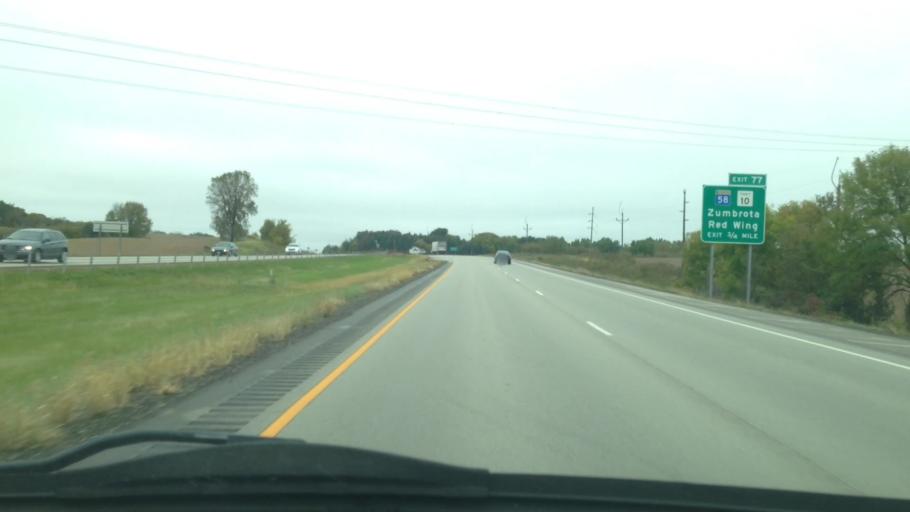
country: US
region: Minnesota
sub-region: Goodhue County
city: Zumbrota
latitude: 44.2728
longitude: -92.6563
